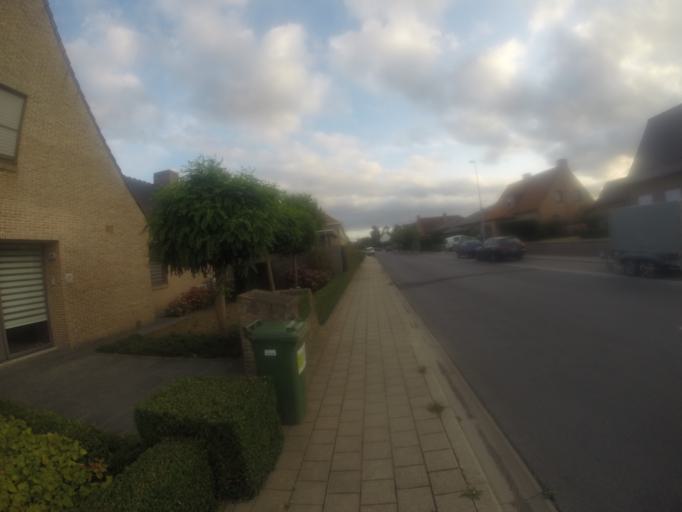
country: BE
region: Flanders
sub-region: Provincie West-Vlaanderen
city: Poperinge
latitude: 50.8621
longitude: 2.7242
